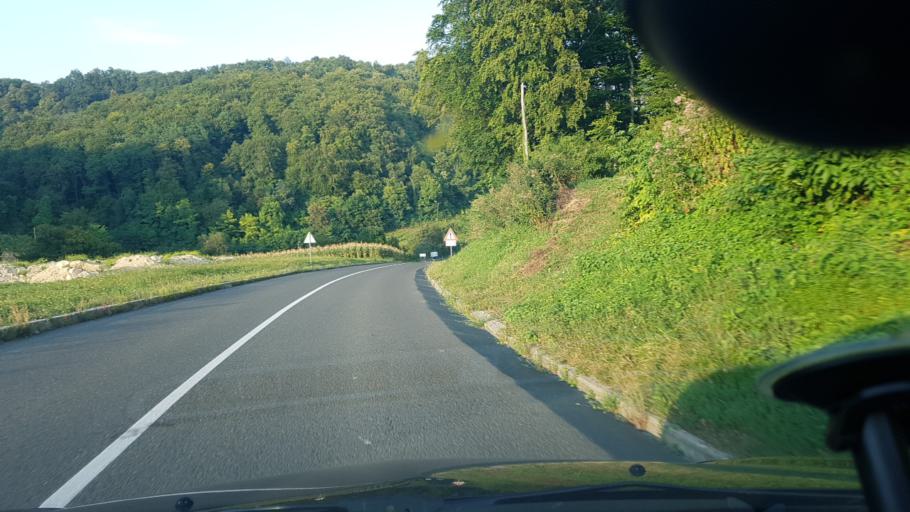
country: HR
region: Krapinsko-Zagorska
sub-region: Grad Krapina
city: Krapina
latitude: 46.1684
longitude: 15.8454
